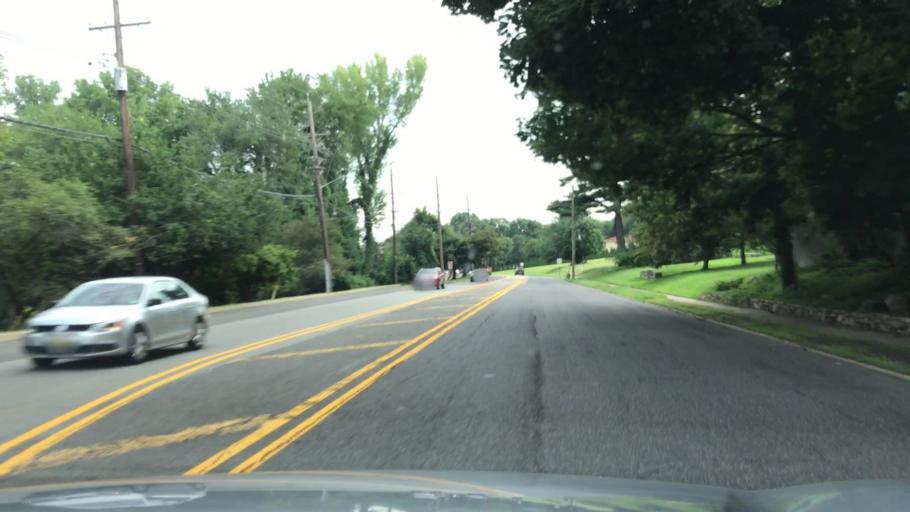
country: US
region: New Jersey
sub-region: Bergen County
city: Oradell
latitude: 40.9663
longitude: -74.0302
